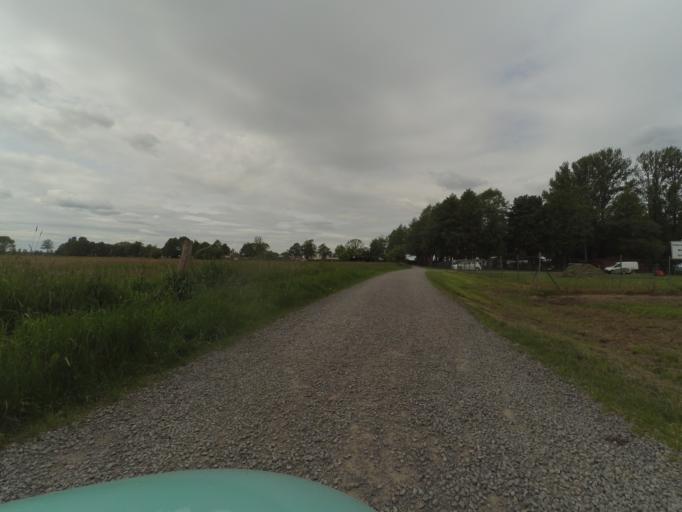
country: DE
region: Lower Saxony
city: Hagenburg
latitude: 52.4509
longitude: 9.3499
